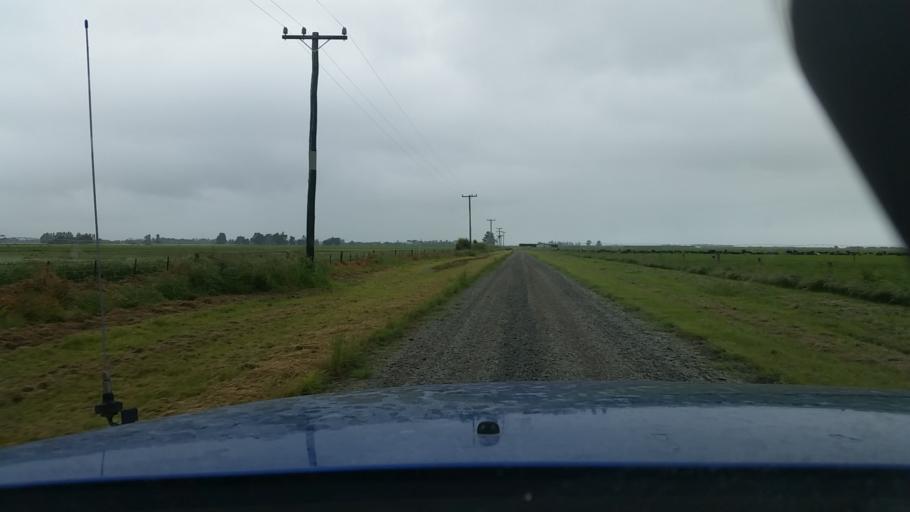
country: NZ
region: Canterbury
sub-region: Ashburton District
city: Tinwald
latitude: -44.0485
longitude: 171.6325
